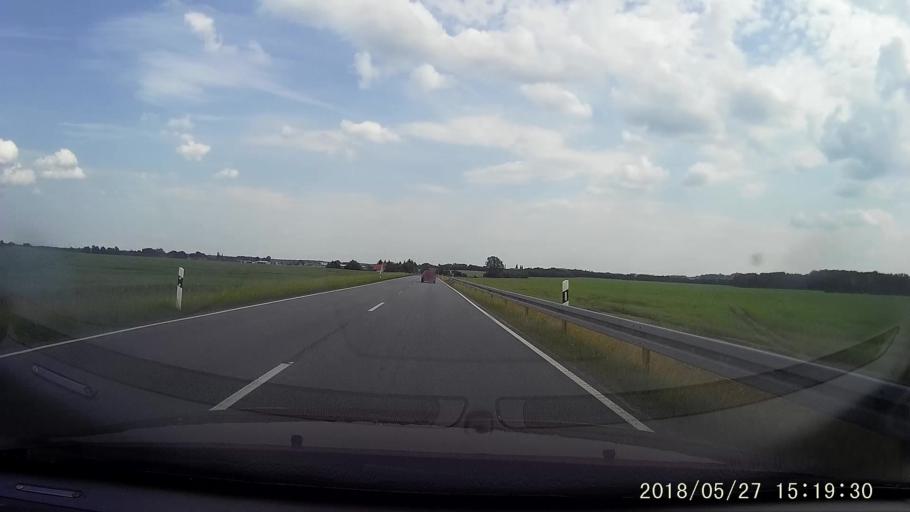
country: DE
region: Saxony
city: Kodersdorf
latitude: 51.2551
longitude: 14.8730
